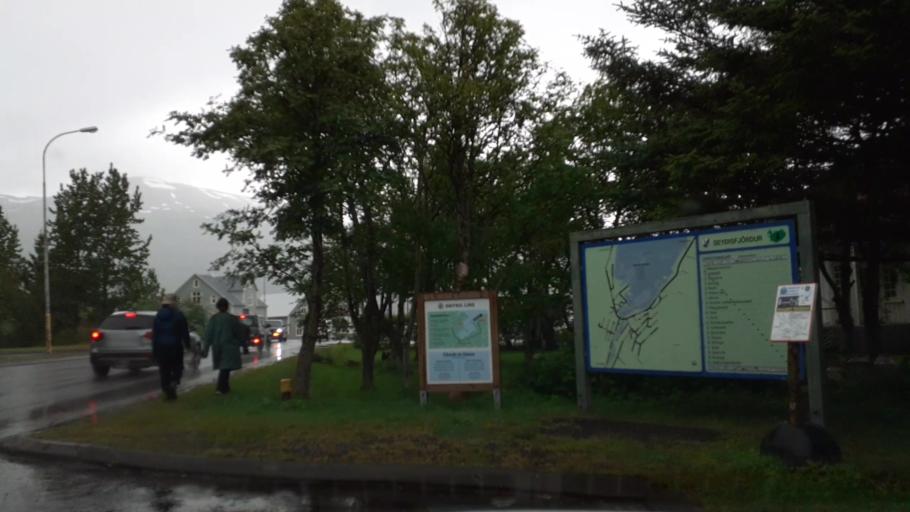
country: IS
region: East
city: Eskifjoerdur
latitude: 65.2594
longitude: -14.0102
